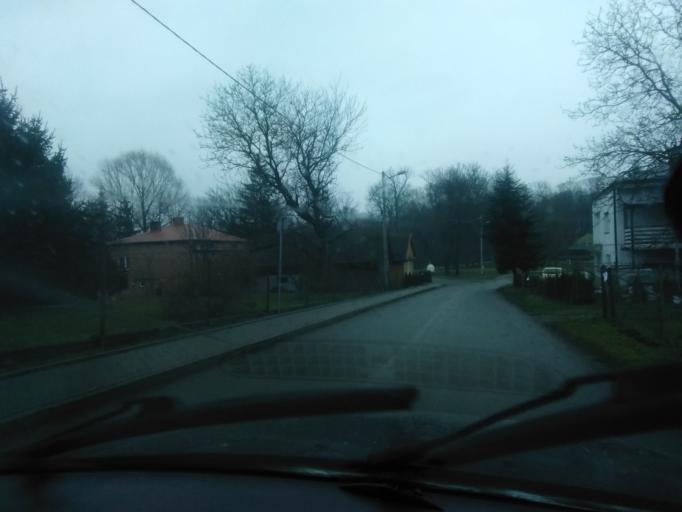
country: PL
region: Subcarpathian Voivodeship
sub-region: Powiat jaroslawski
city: Rokietnica
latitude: 49.9422
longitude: 22.6141
